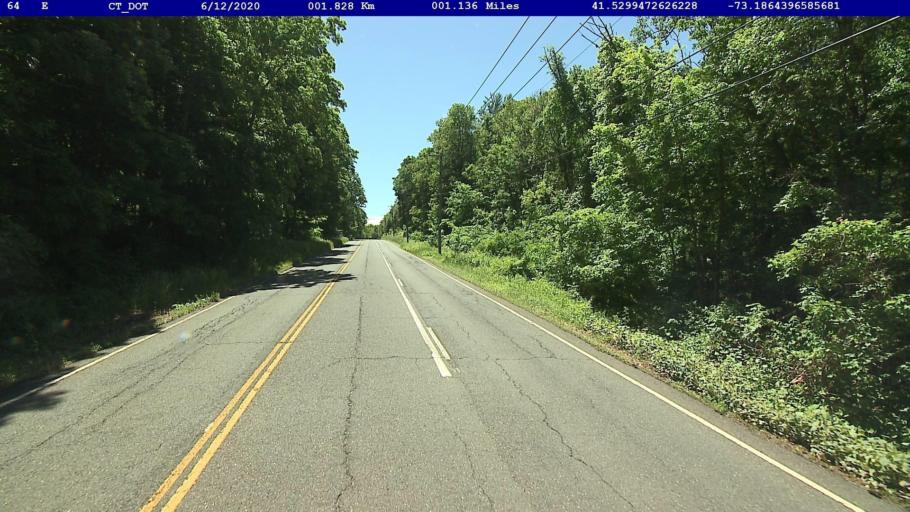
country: US
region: Connecticut
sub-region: Litchfield County
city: Woodbury Center
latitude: 41.5295
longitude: -73.1866
